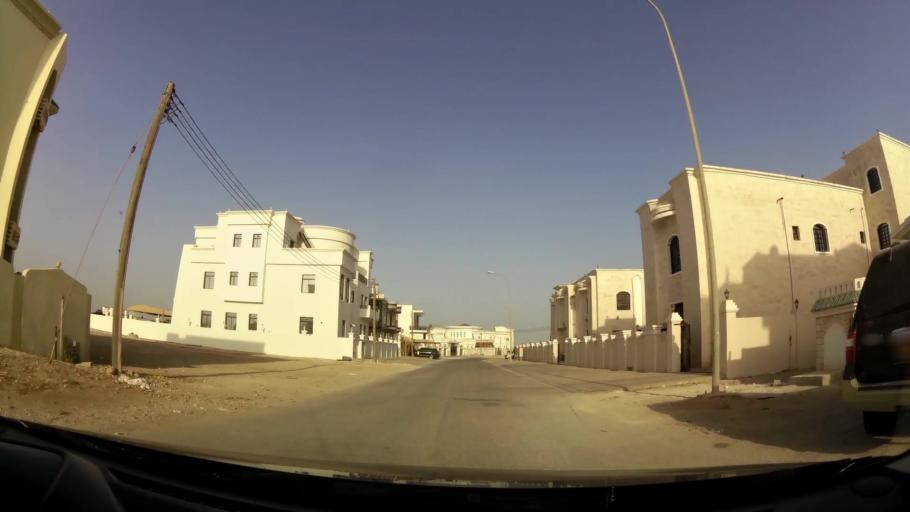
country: OM
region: Zufar
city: Salalah
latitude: 17.0017
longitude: 54.0281
